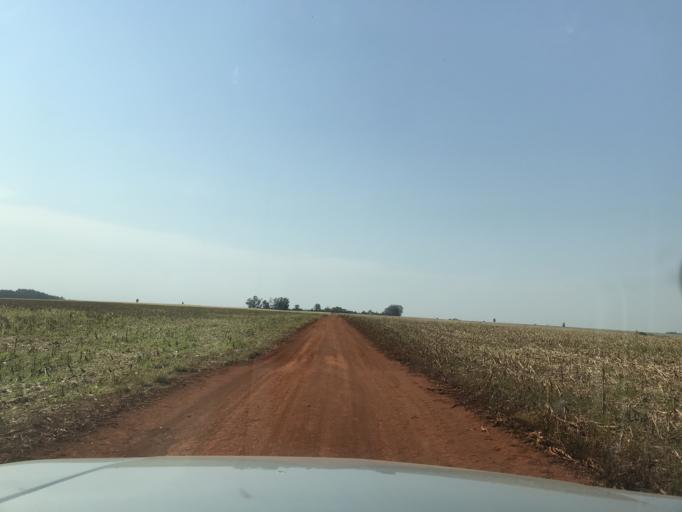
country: BR
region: Parana
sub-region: Palotina
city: Palotina
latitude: -24.2412
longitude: -53.7222
